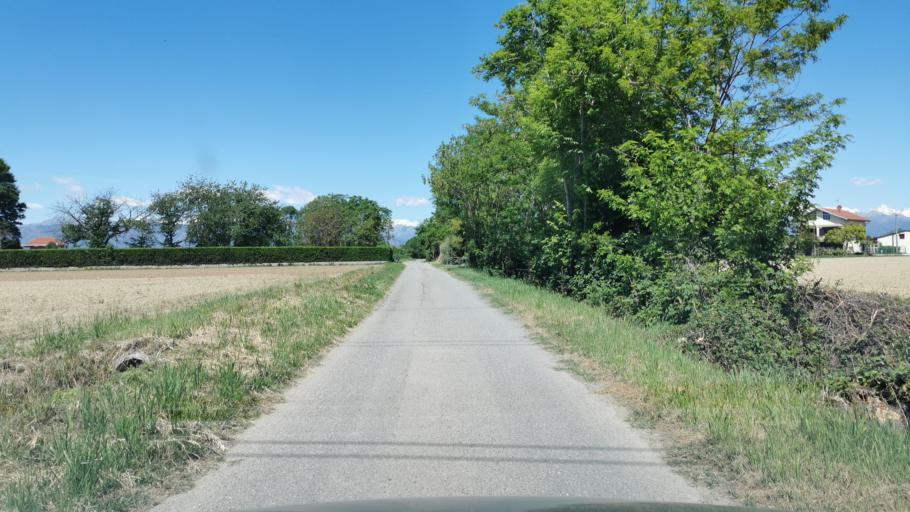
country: IT
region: Piedmont
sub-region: Provincia di Torino
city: Leini
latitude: 45.1706
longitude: 7.7234
